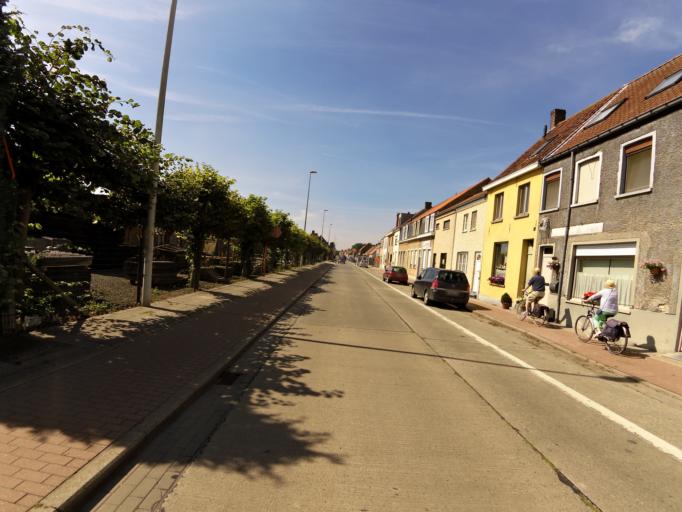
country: BE
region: Flanders
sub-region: Provincie West-Vlaanderen
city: Sint-Kruis
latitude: 51.2410
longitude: 3.2487
